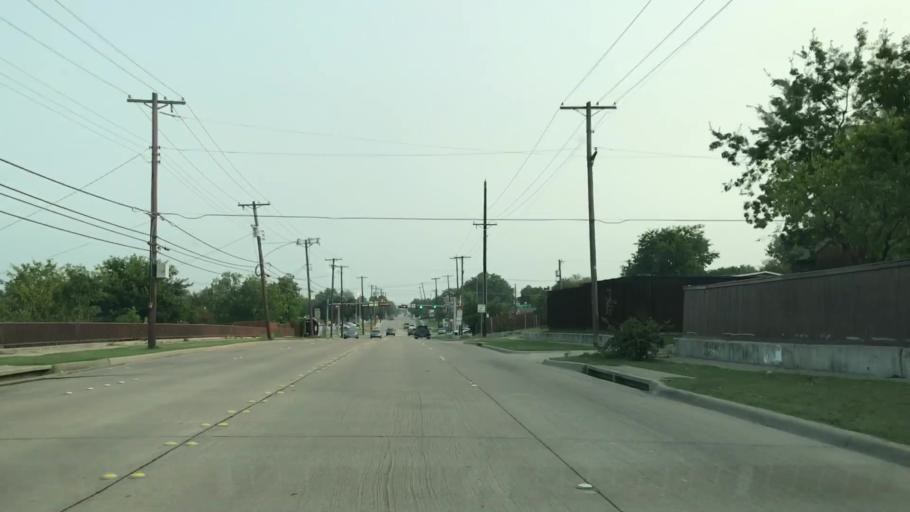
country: US
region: Texas
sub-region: Dallas County
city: Garland
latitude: 32.8958
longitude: -96.6222
